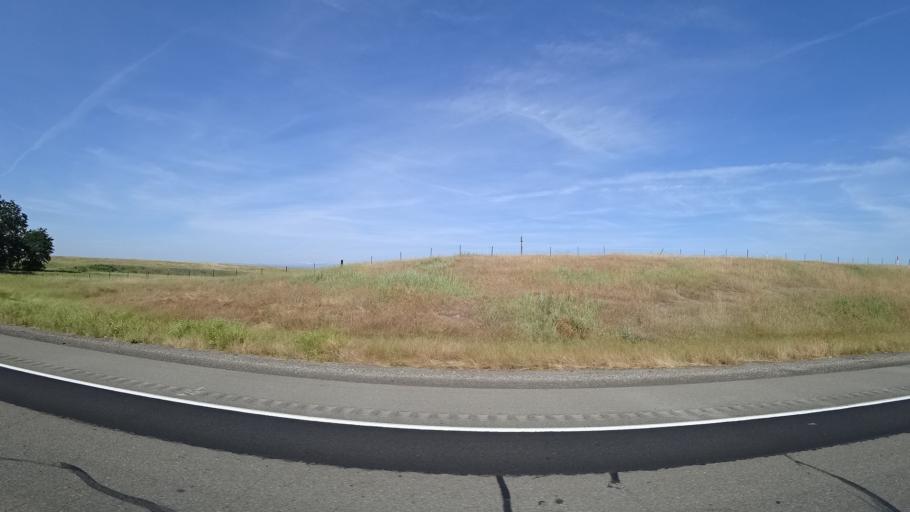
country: US
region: California
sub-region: Tehama County
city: Los Molinos
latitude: 39.9517
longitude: -122.0570
